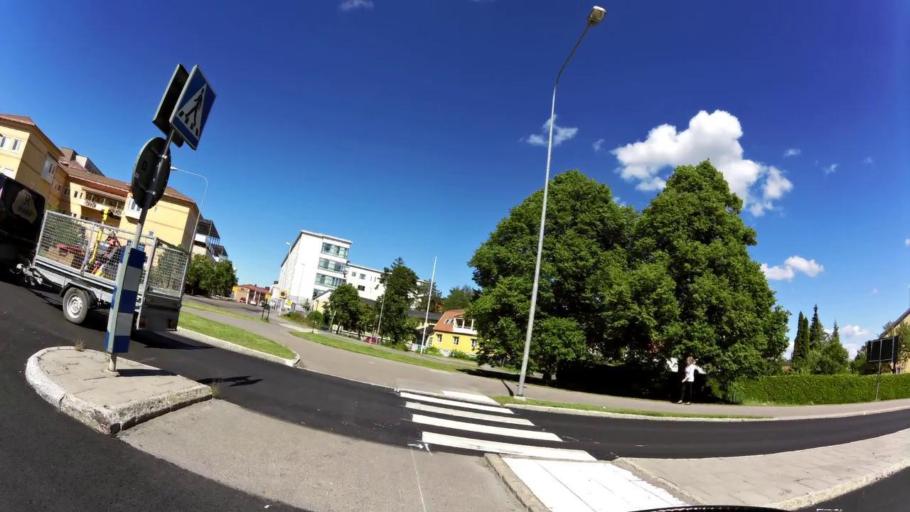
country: SE
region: OEstergoetland
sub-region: Linkopings Kommun
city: Linkoping
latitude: 58.3993
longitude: 15.6209
